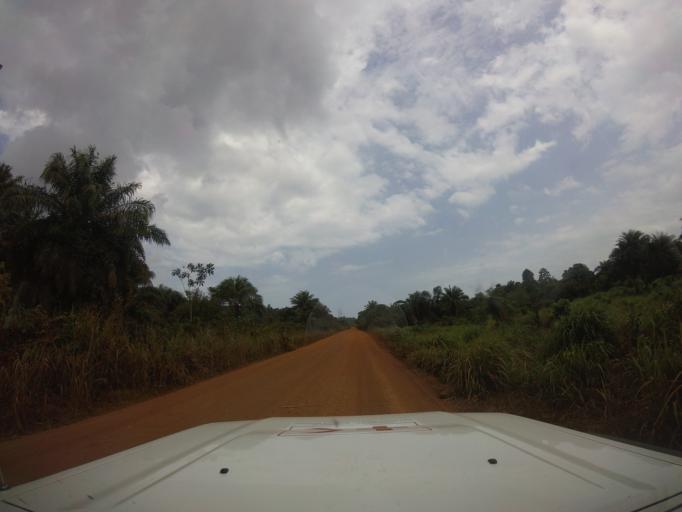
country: LR
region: Grand Cape Mount
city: Robertsport
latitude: 6.7471
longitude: -11.3522
